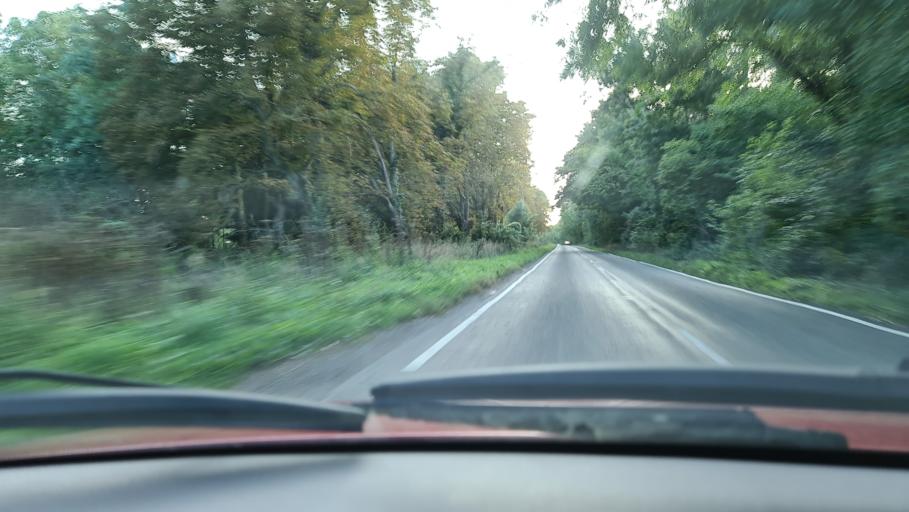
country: GB
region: England
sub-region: Oxfordshire
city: Somerton
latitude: 51.8933
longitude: -1.2343
